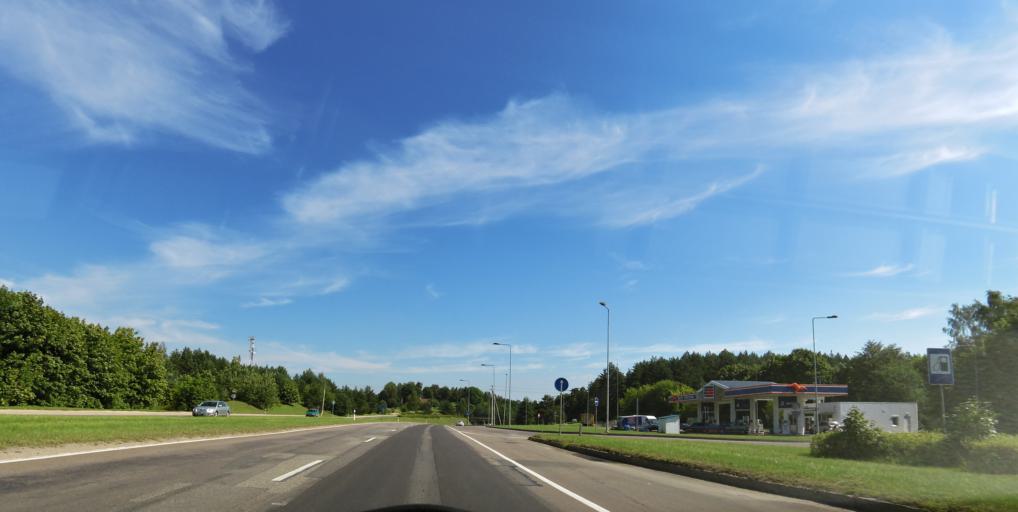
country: LT
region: Vilnius County
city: Rasos
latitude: 54.6922
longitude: 25.3453
